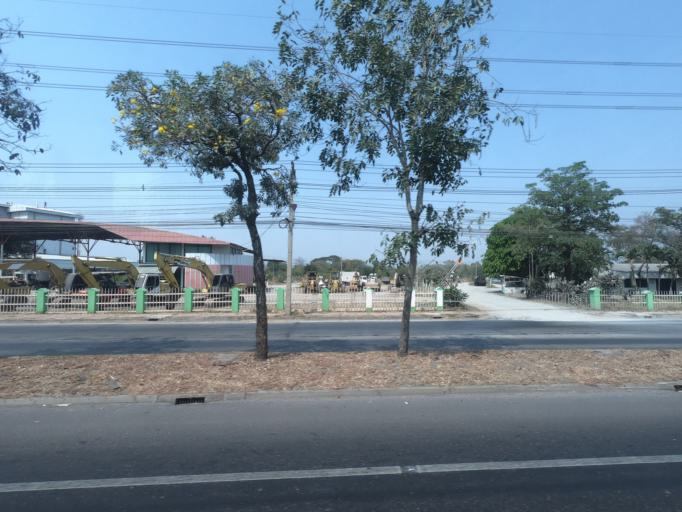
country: TH
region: Nakhon Ratchasima
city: Kham Thale So
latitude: 14.9310
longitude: 101.9755
